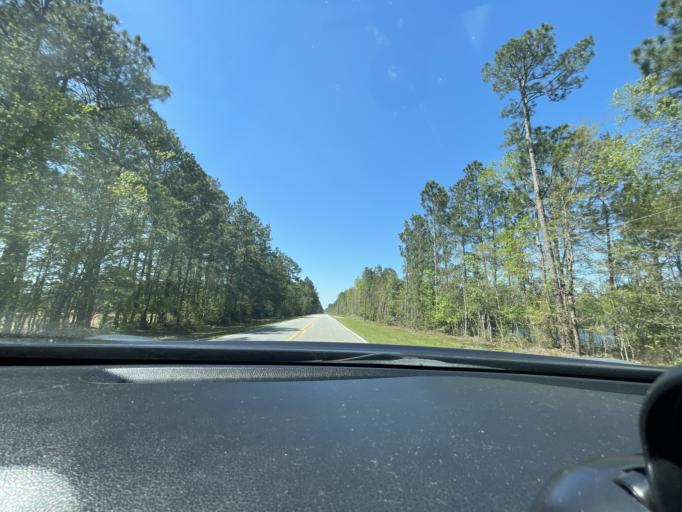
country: US
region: Georgia
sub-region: Chatham County
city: Bloomingdale
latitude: 32.0959
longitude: -81.2982
